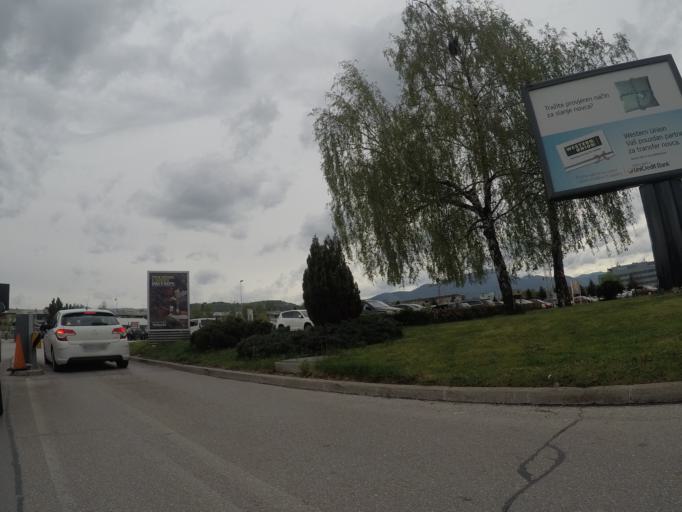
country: BA
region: Federation of Bosnia and Herzegovina
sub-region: Kanton Sarajevo
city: Sarajevo
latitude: 43.8268
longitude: 18.3364
